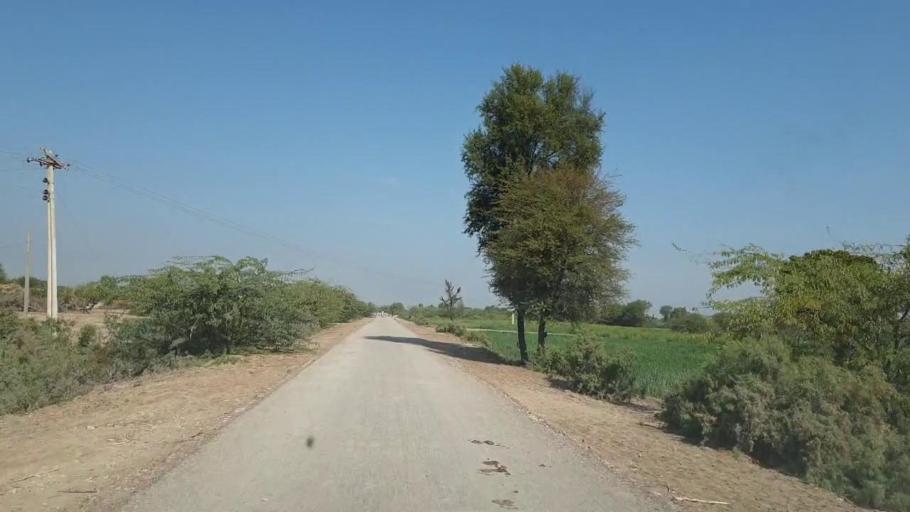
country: PK
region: Sindh
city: Mirpur Khas
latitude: 25.6221
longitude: 69.0875
